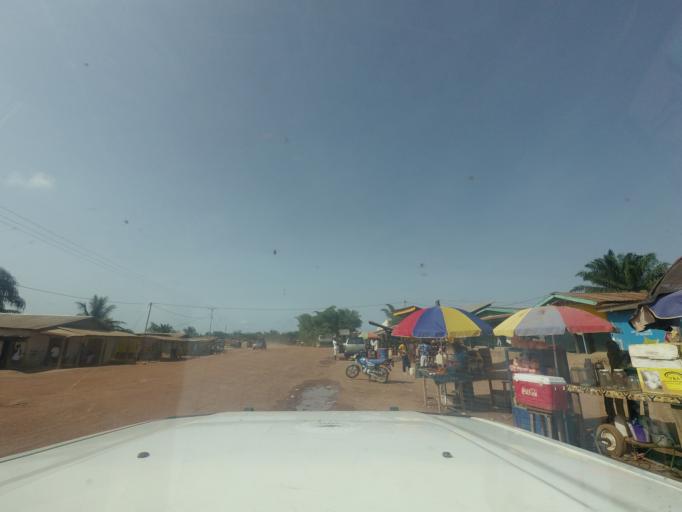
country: LR
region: Nimba
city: Sanniquellie
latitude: 7.2168
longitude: -8.9762
